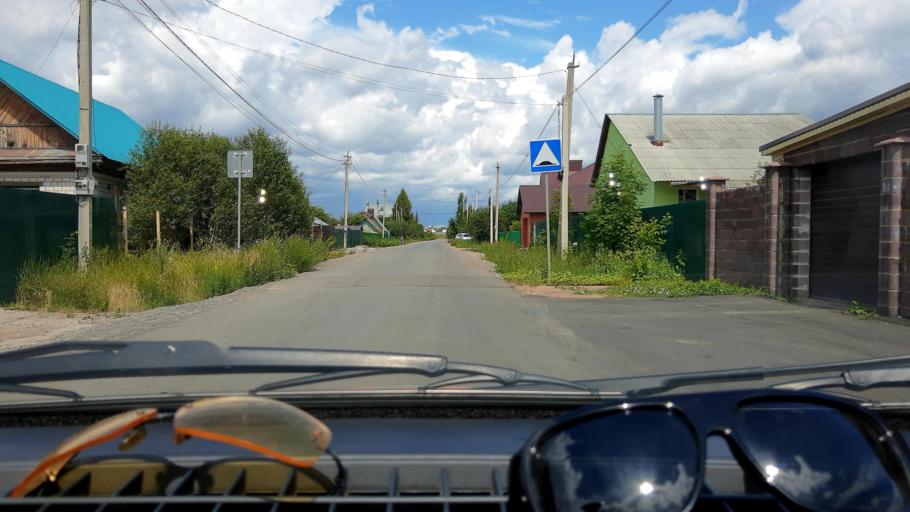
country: RU
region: Bashkortostan
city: Ufa
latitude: 54.6417
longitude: 55.9228
